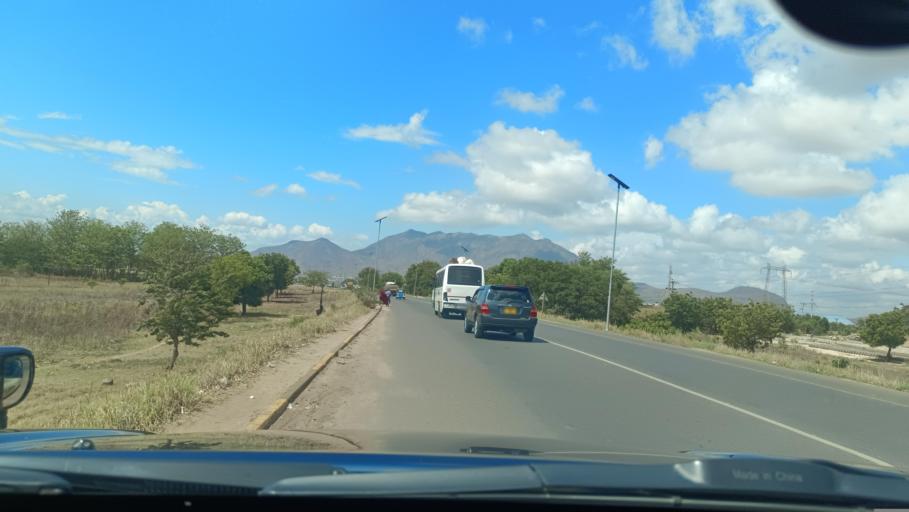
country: TZ
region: Morogoro
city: Morogoro
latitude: -6.8070
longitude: 37.6560
